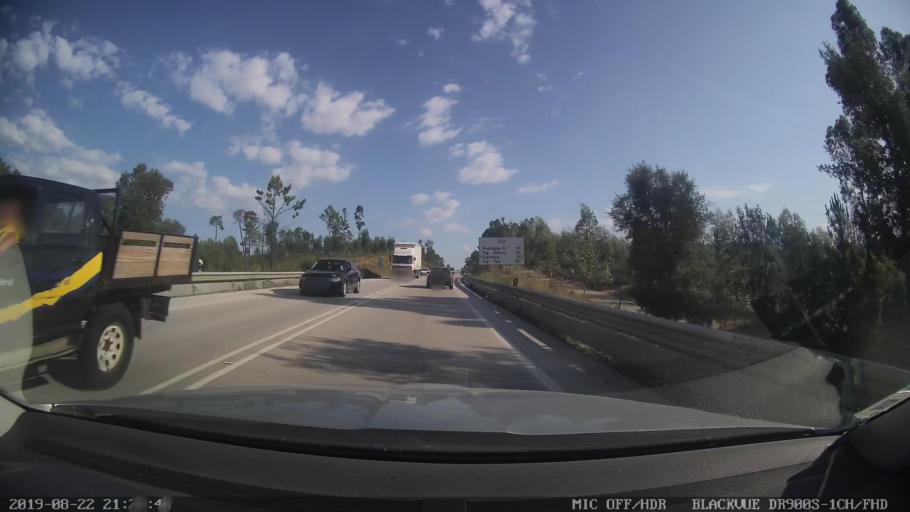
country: PT
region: Castelo Branco
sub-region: Serta
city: Serta
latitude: 39.8439
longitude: -8.1243
